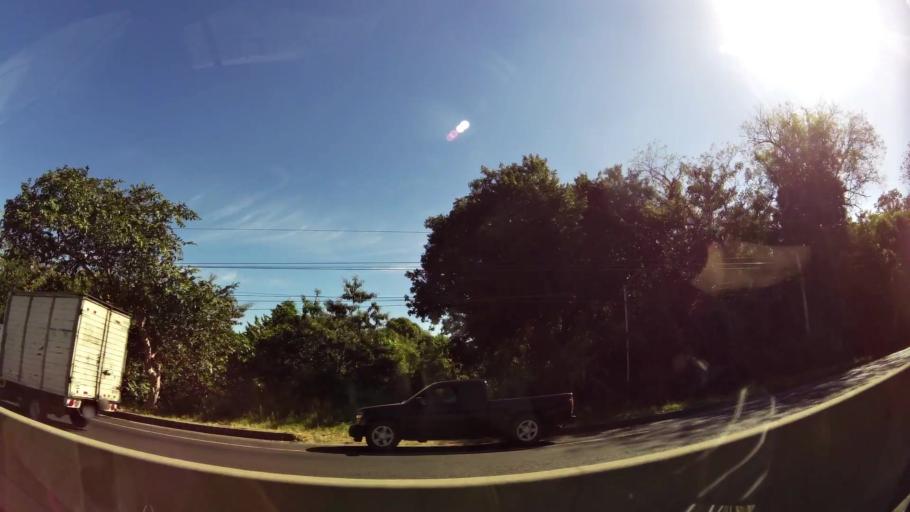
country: SV
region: Santa Ana
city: Coatepeque
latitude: 13.9248
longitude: -89.5200
